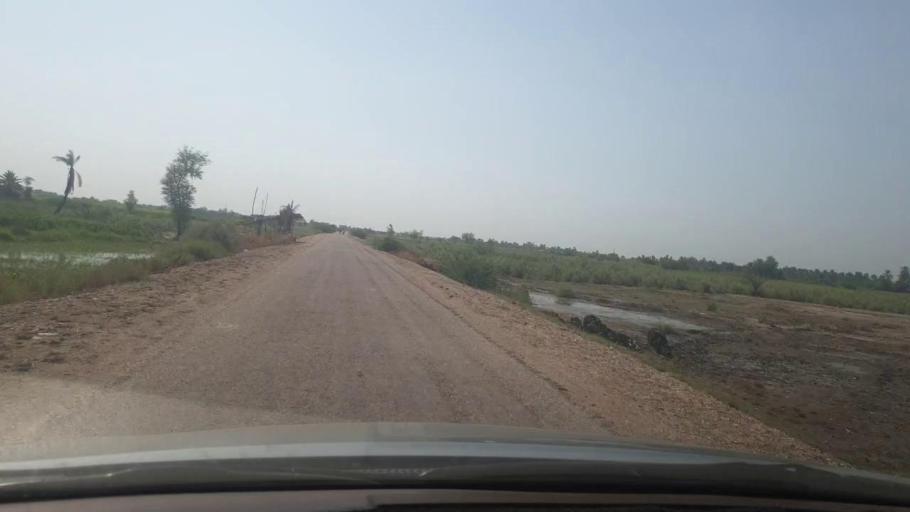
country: PK
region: Sindh
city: Ranipur
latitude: 27.2638
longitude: 68.5821
